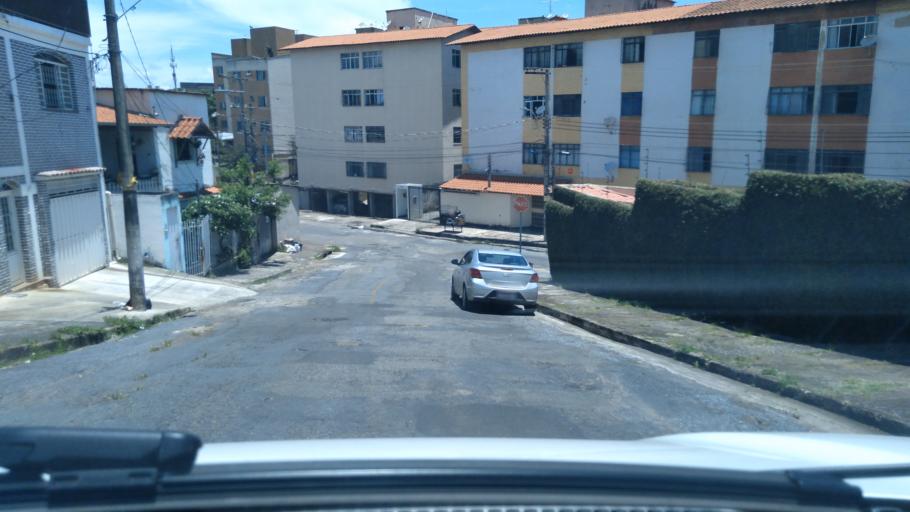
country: BR
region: Minas Gerais
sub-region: Contagem
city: Contagem
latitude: -19.9306
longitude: -43.9964
